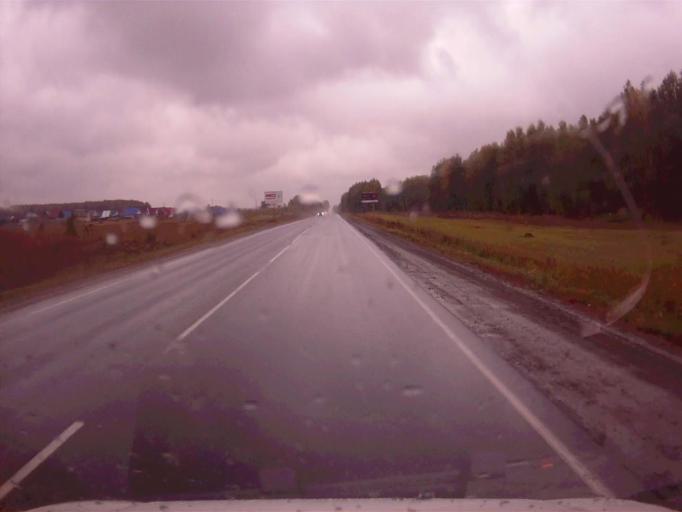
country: RU
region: Chelyabinsk
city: Argayash
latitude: 55.4197
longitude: 61.0189
